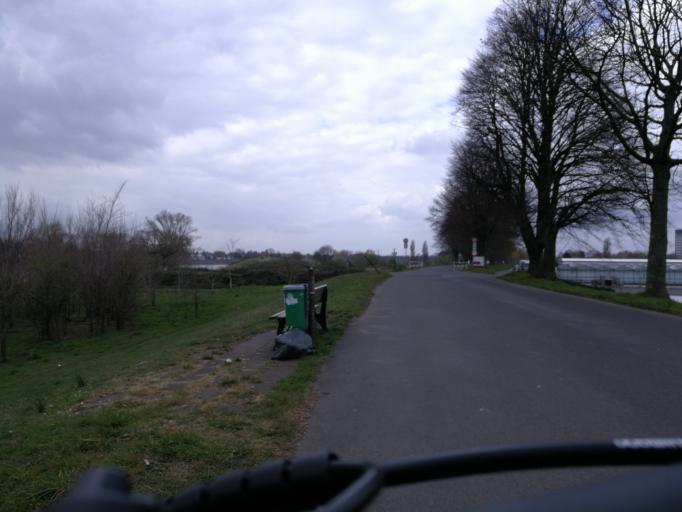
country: DE
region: North Rhine-Westphalia
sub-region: Regierungsbezirk Dusseldorf
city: Dusseldorf
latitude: 51.1840
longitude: 6.7498
